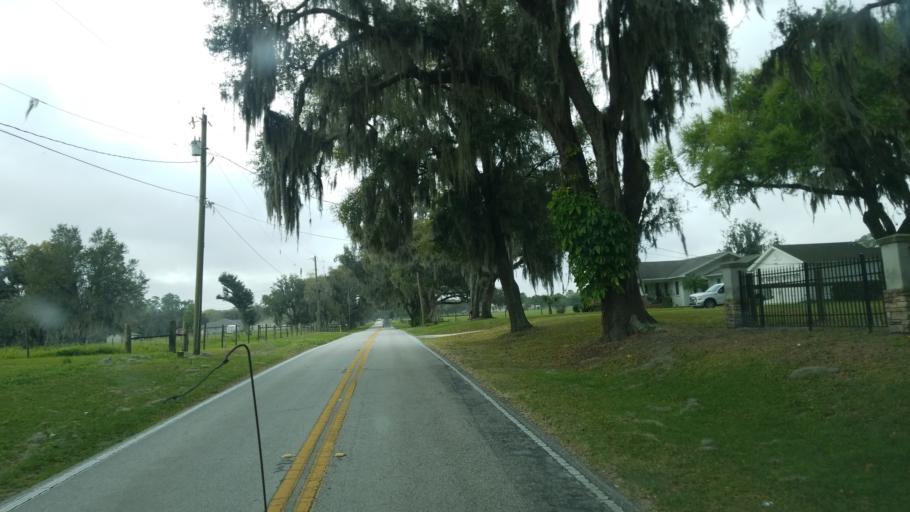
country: US
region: Florida
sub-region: Polk County
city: Kathleen
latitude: 28.1763
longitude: -82.0150
